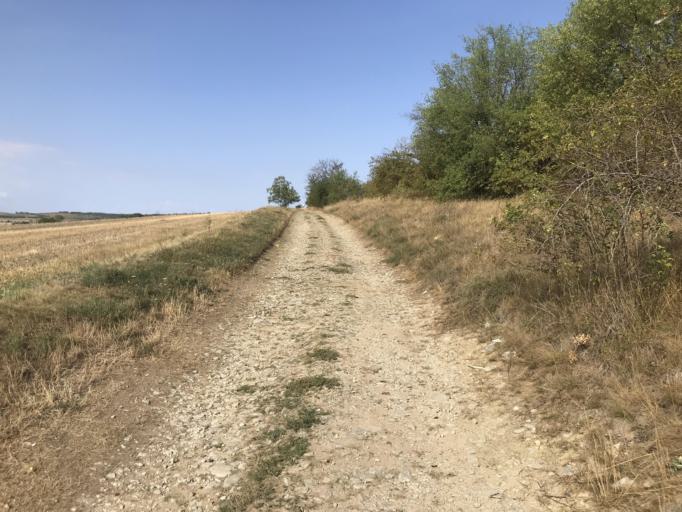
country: DE
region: Saxony-Anhalt
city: Schwanebeck
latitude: 51.9733
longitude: 11.1169
